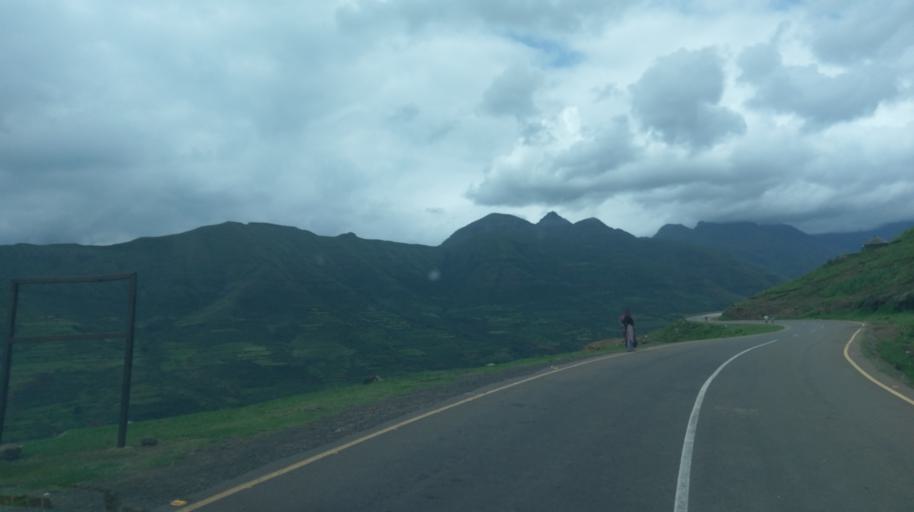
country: LS
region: Butha-Buthe
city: Butha-Buthe
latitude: -29.0360
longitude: 28.2972
